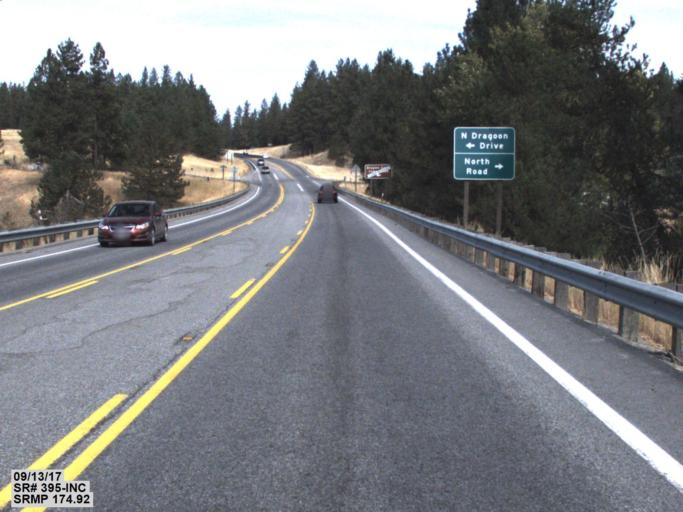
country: US
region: Washington
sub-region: Spokane County
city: Deer Park
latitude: 47.8865
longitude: -117.4241
